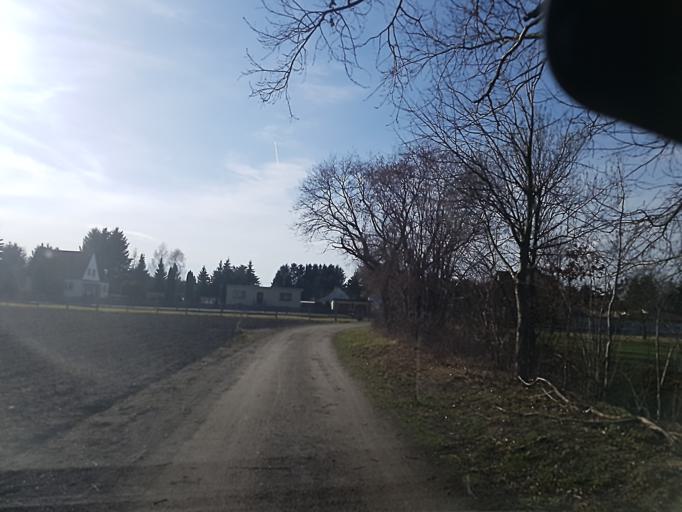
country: DE
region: Brandenburg
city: Schonborn
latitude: 51.5980
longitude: 13.4983
